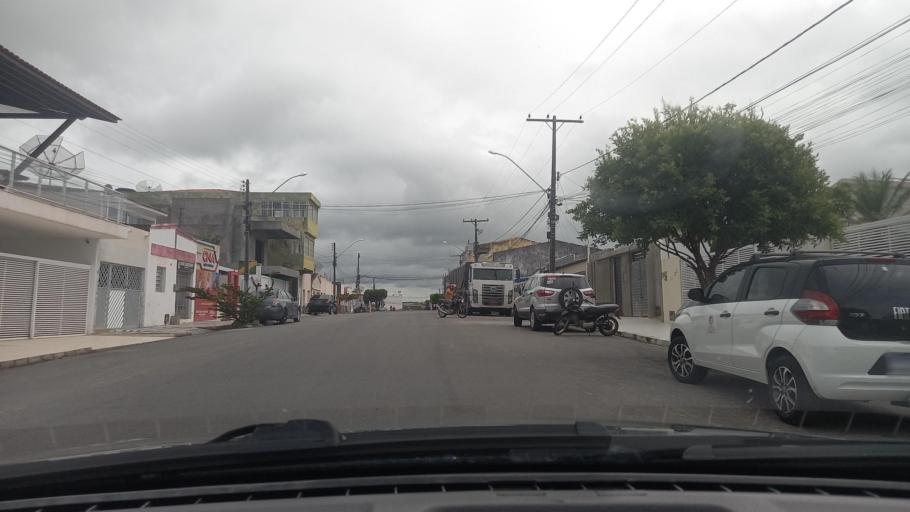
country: BR
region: Alagoas
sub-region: Delmiro Gouveia
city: Delmiro Gouveia
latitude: -9.3856
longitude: -37.9989
